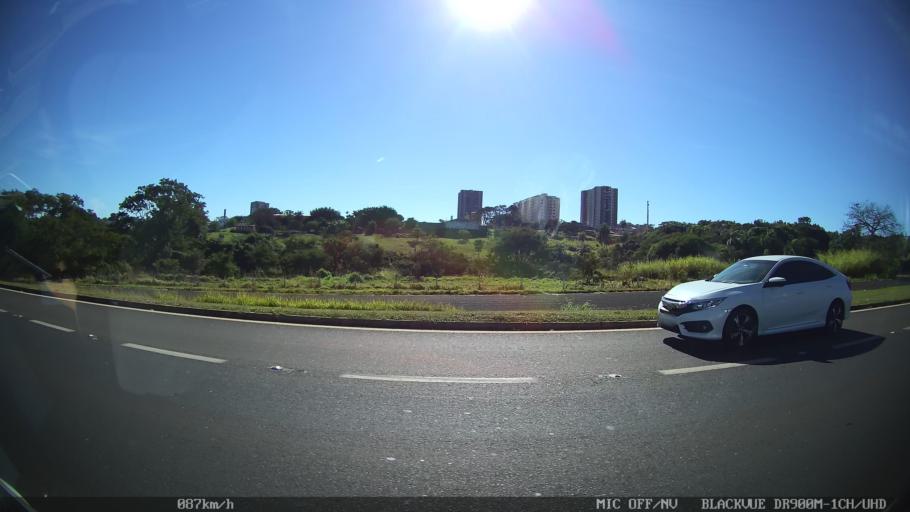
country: BR
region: Sao Paulo
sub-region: Franca
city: Franca
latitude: -20.5671
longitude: -47.4073
